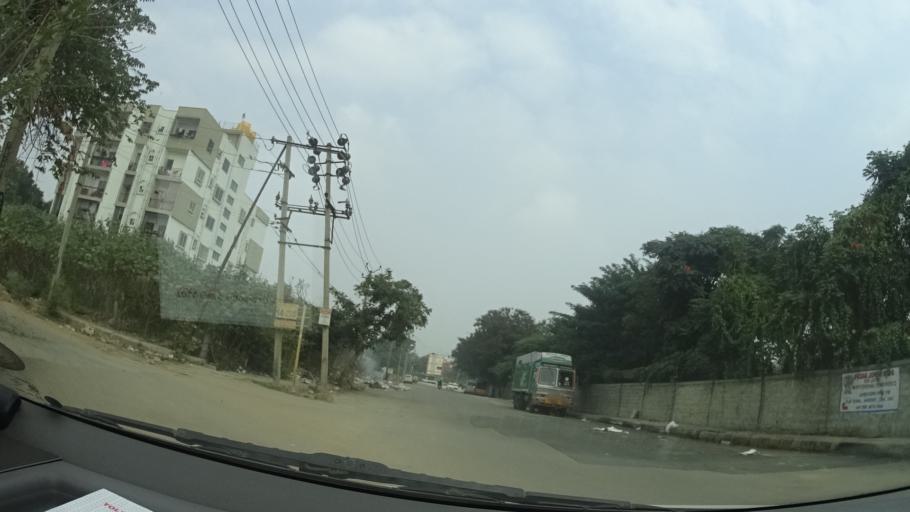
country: IN
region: Karnataka
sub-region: Bangalore Urban
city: Yelahanka
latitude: 13.0364
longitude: 77.6256
